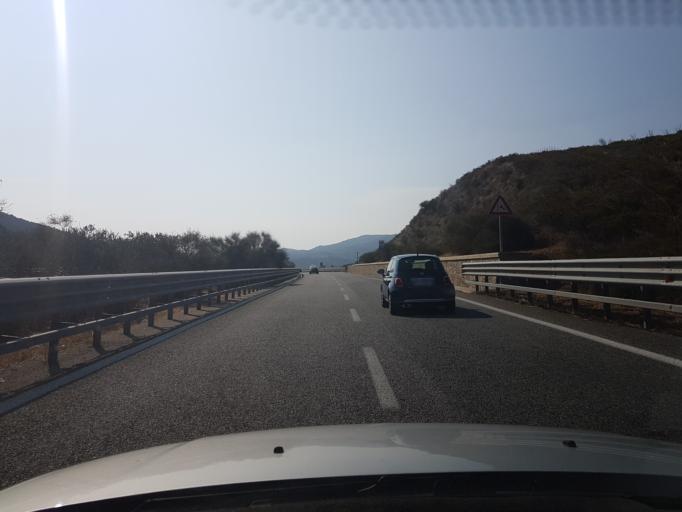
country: IT
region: Sardinia
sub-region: Provincia di Olbia-Tempio
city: San Teodoro
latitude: 40.7745
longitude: 9.6250
